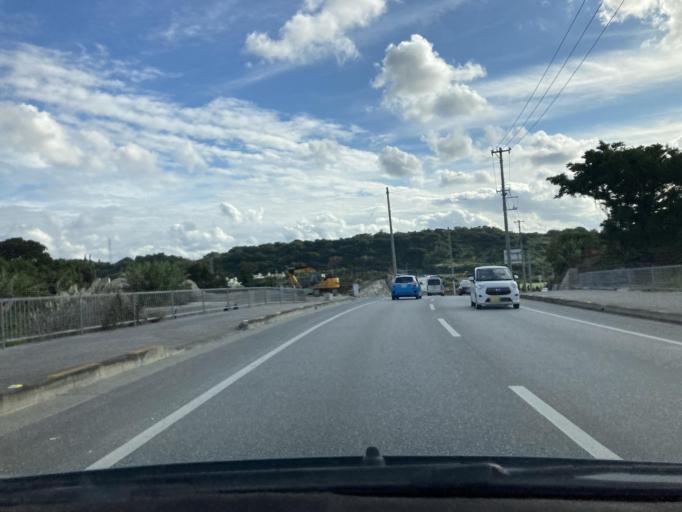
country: JP
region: Okinawa
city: Itoman
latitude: 26.1298
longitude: 127.6838
